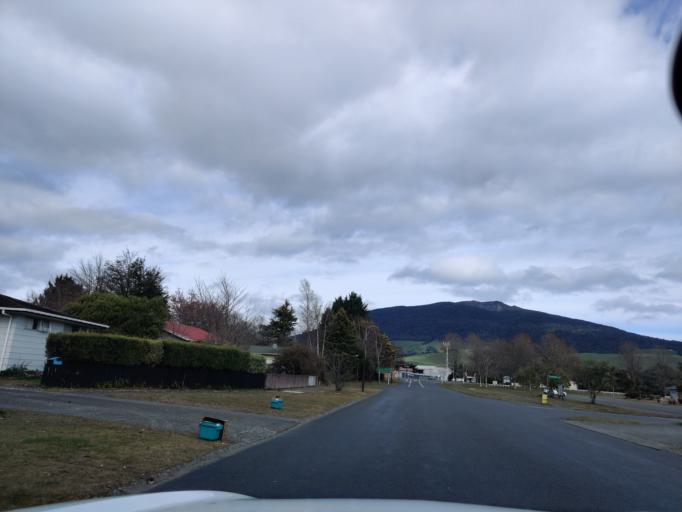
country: NZ
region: Waikato
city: Turangi
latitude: -38.9939
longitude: 175.8035
